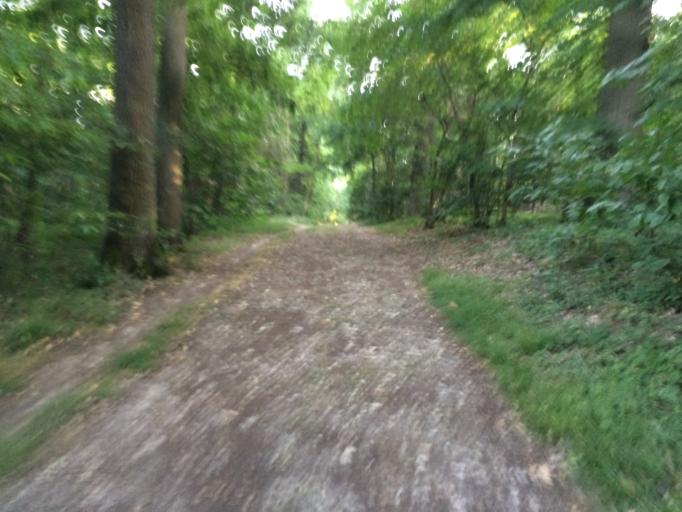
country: FR
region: Ile-de-France
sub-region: Departement de l'Essonne
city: Igny
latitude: 48.7451
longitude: 2.2398
